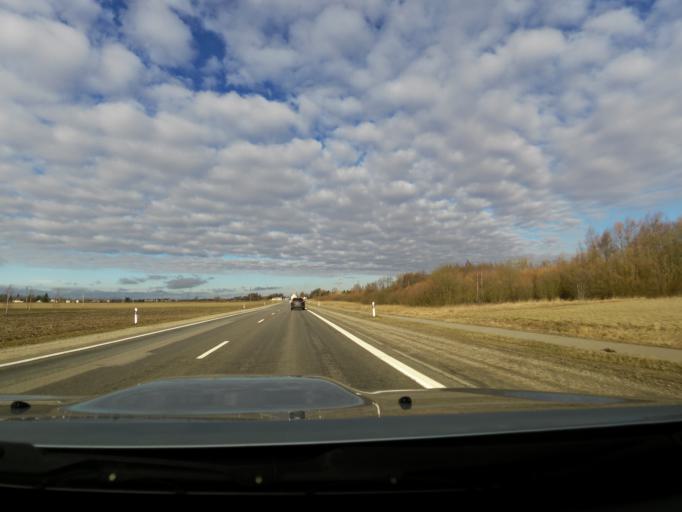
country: LT
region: Panevezys
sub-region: Panevezys City
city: Panevezys
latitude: 55.7412
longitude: 24.1855
